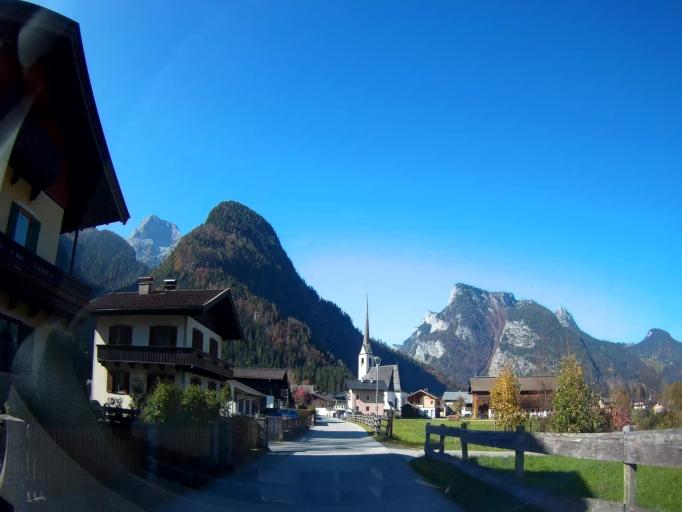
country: AT
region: Salzburg
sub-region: Politischer Bezirk Zell am See
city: Sankt Martin bei Lofer
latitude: 47.5650
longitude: 12.7093
